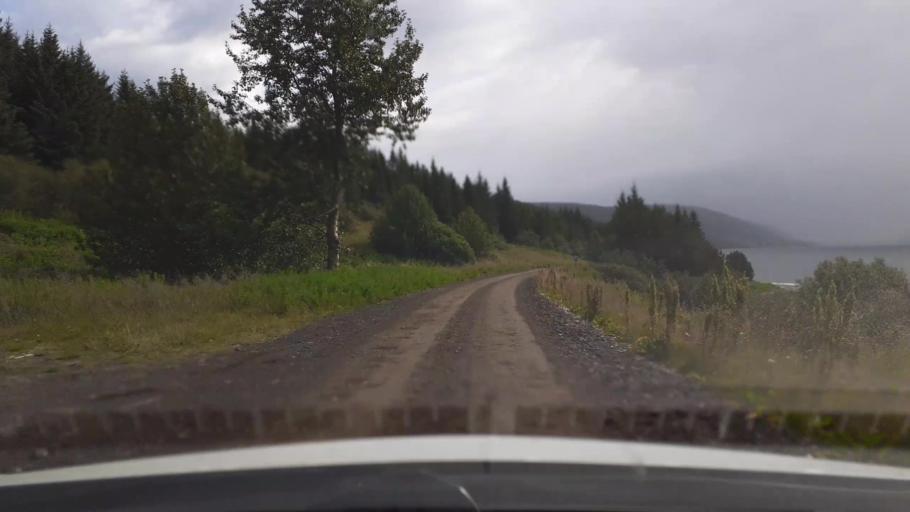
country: IS
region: Capital Region
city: Mosfellsbaer
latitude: 64.5204
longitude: -21.4389
